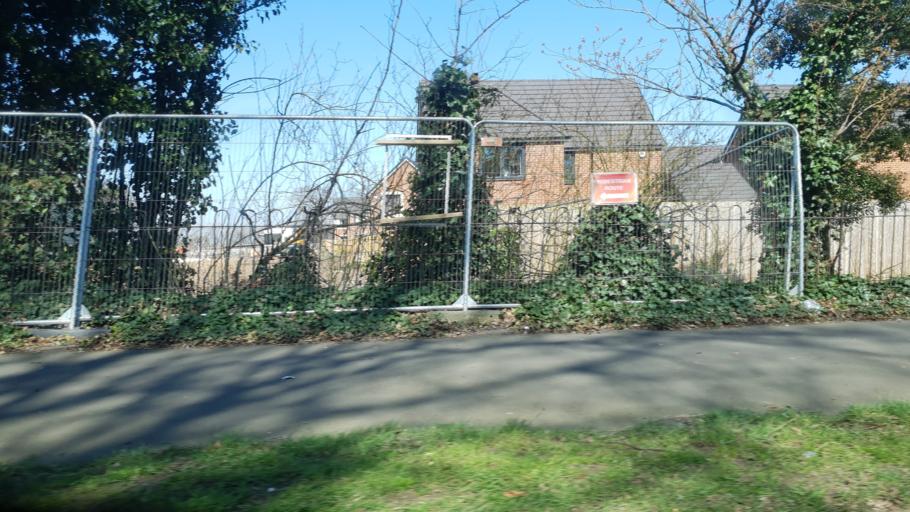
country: GB
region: England
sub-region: Middlesbrough
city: Nunthorpe
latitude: 54.5419
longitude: -1.2080
